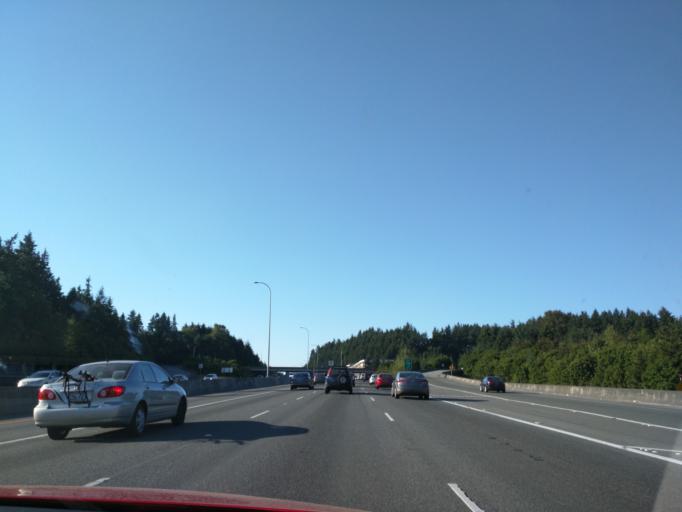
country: US
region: Washington
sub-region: Snohomish County
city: Mountlake Terrace
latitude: 47.7813
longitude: -122.3168
